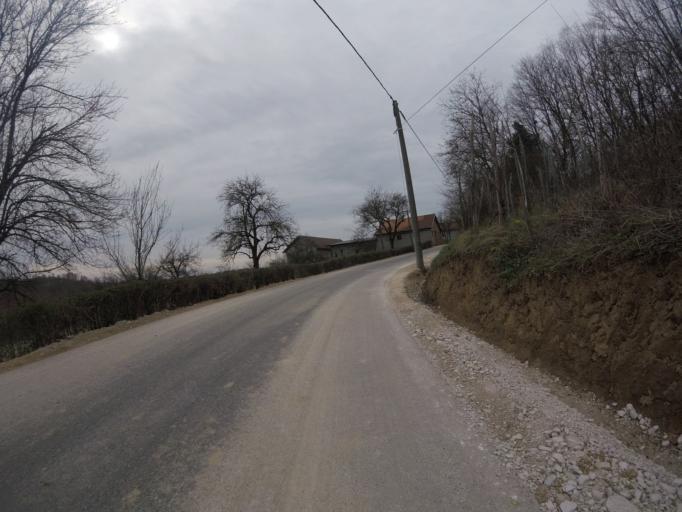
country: HR
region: Grad Zagreb
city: Strmec
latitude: 45.6102
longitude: 15.9120
